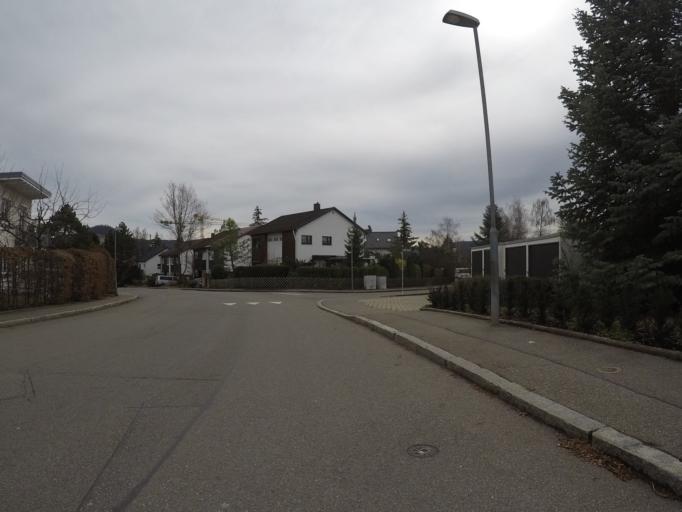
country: DE
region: Baden-Wuerttemberg
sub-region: Tuebingen Region
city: Reutlingen
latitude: 48.5028
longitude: 9.1958
